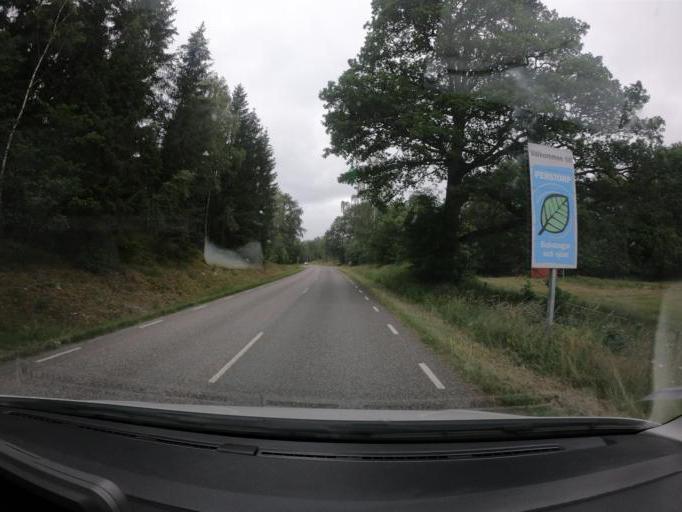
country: SE
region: Skane
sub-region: Perstorps Kommun
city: Perstorp
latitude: 56.1152
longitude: 13.4140
